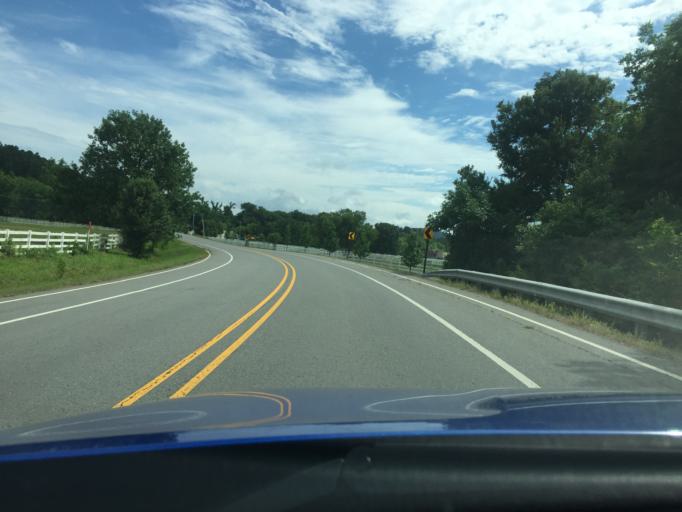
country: US
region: Arkansas
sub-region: Pulaski County
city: Maumelle
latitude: 34.8160
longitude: -92.4427
